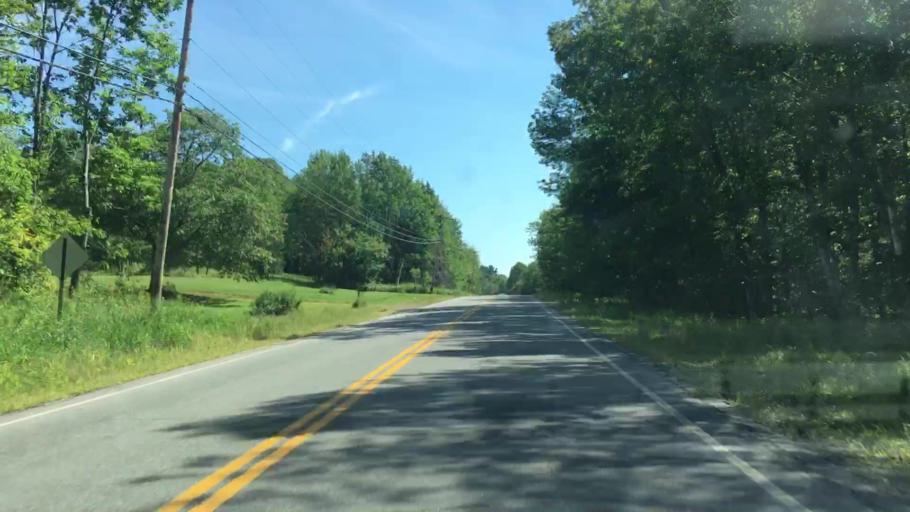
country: US
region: Maine
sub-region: Piscataquis County
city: Milo
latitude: 45.1977
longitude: -68.9045
